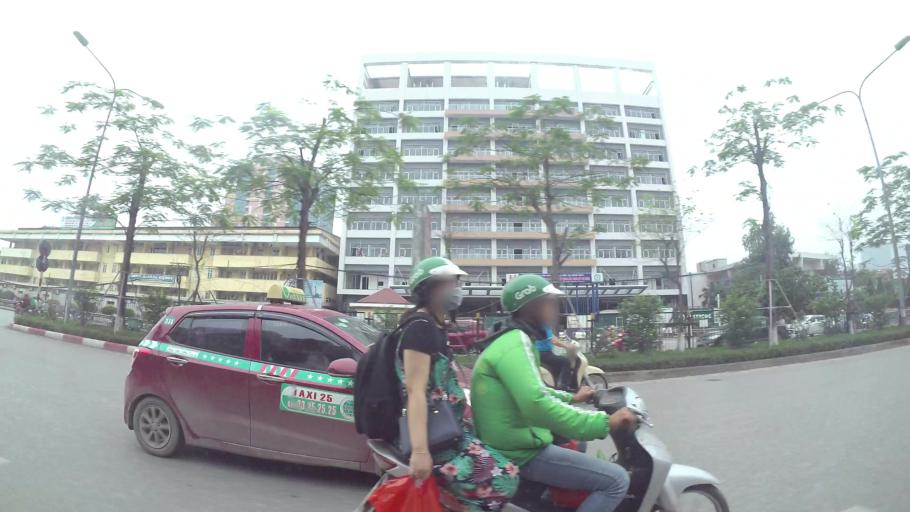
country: VN
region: Ha Noi
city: Hai BaTrung
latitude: 21.0033
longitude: 105.8415
